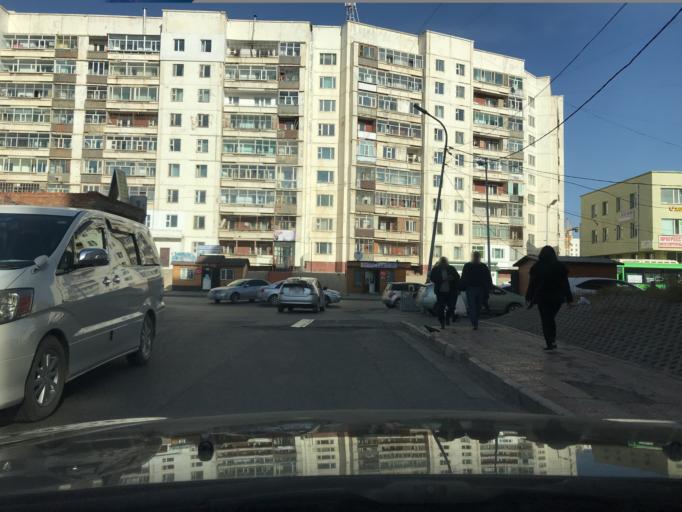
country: MN
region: Ulaanbaatar
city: Ulaanbaatar
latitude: 47.9124
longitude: 106.9383
